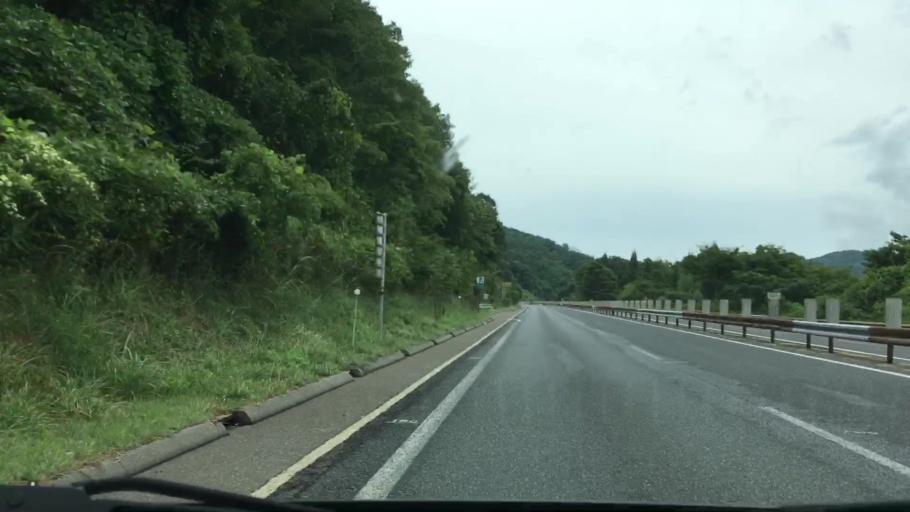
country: JP
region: Okayama
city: Niimi
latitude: 34.9761
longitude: 133.6196
